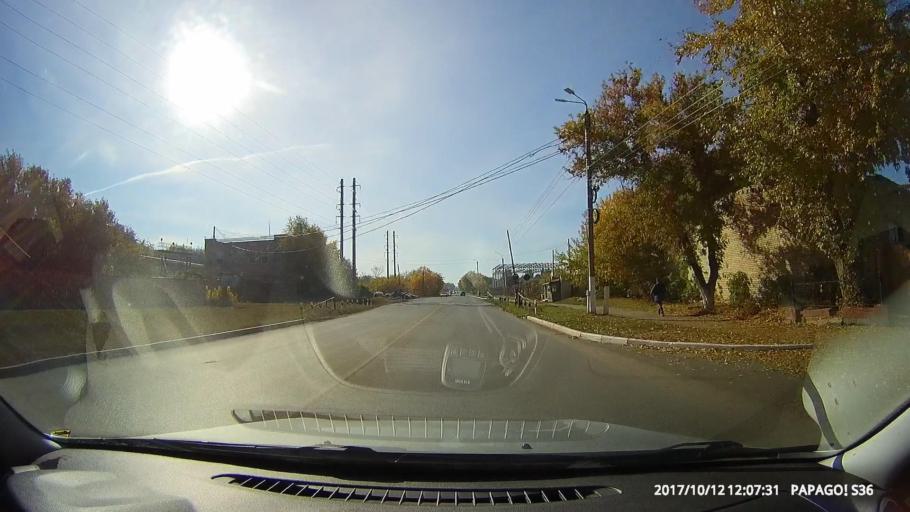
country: RU
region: Samara
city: Chapayevsk
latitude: 52.9667
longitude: 49.7009
